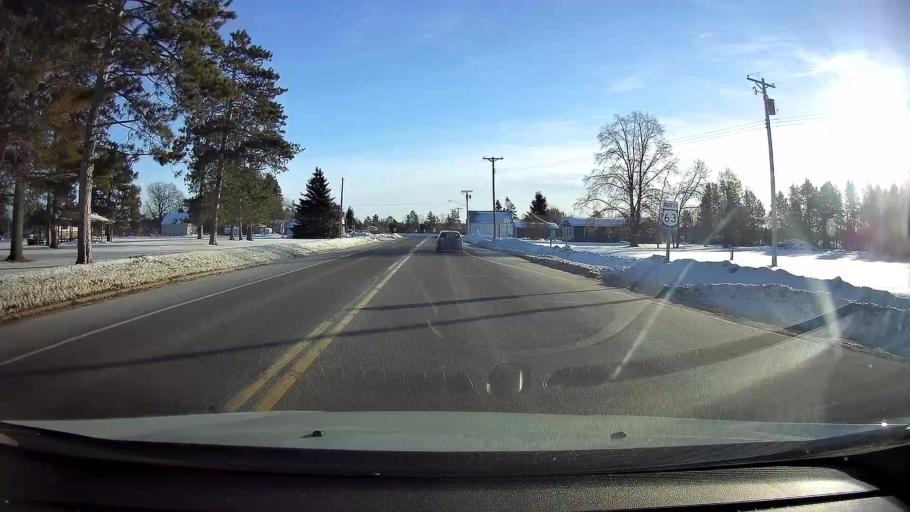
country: US
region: Wisconsin
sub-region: Washburn County
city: Spooner
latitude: 45.9104
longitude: -91.7638
